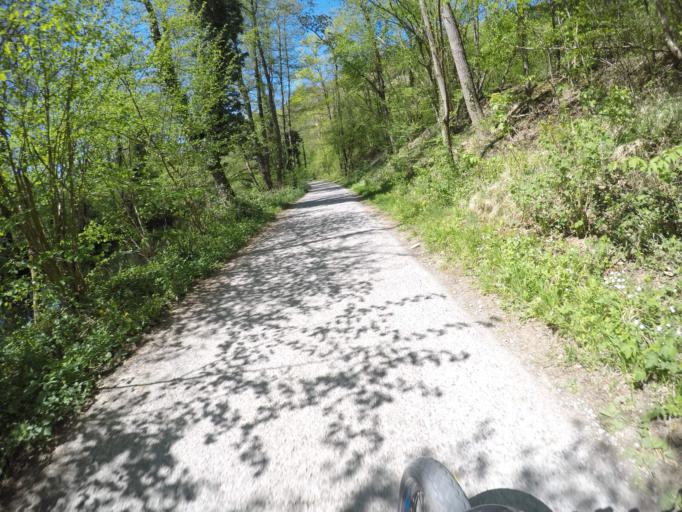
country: DE
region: Baden-Wuerttemberg
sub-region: Regierungsbezirk Stuttgart
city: Waiblingen
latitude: 48.8676
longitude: 9.2874
